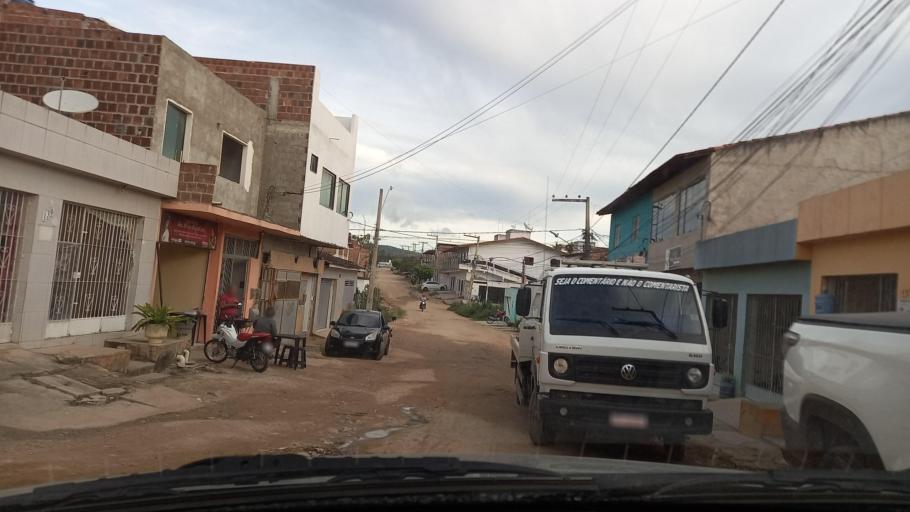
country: BR
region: Pernambuco
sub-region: Gravata
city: Gravata
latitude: -8.1942
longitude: -35.5800
